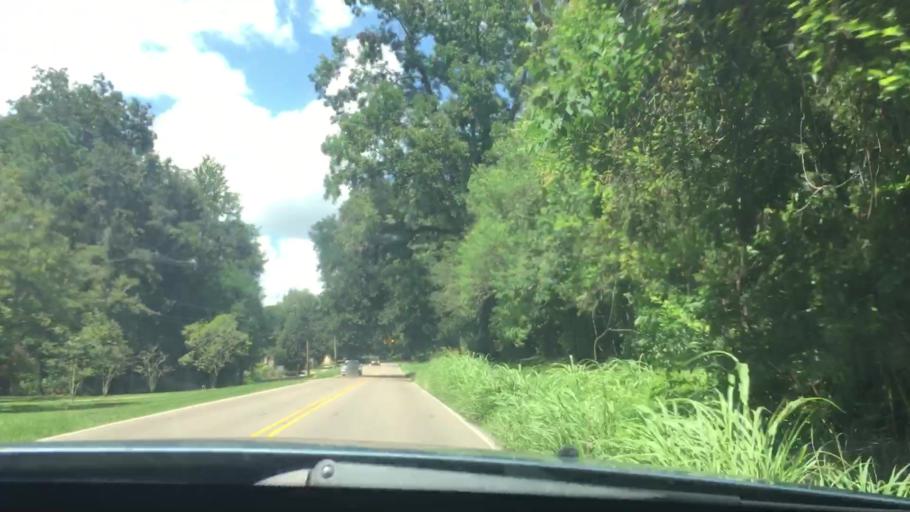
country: US
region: Louisiana
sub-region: East Baton Rouge Parish
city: Oak Hills Place
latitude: 30.3632
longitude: -91.1139
